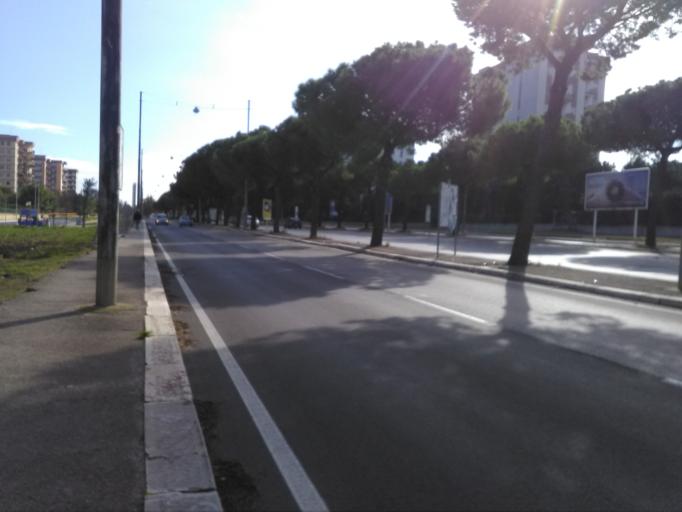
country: IT
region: Apulia
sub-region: Provincia di Bari
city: Triggiano
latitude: 41.1050
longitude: 16.9032
